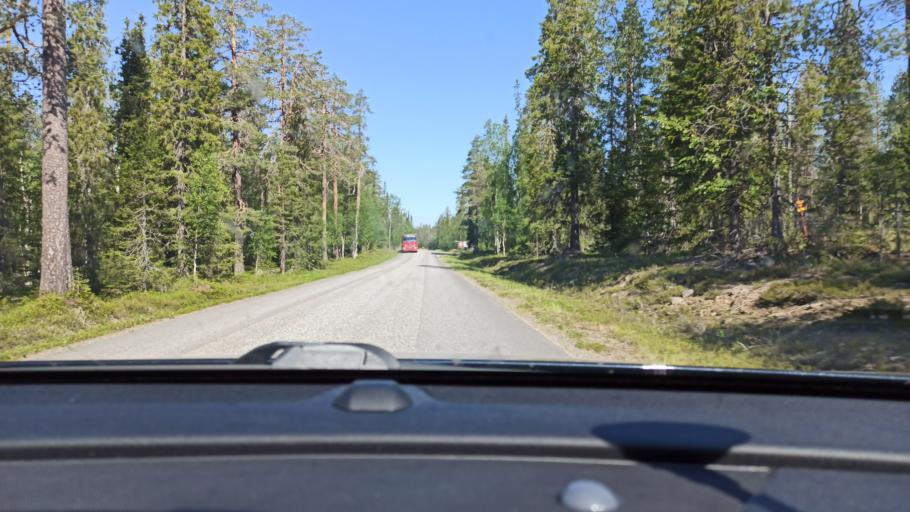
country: FI
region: Lapland
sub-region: Tunturi-Lappi
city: Kolari
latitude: 67.6643
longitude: 24.1623
